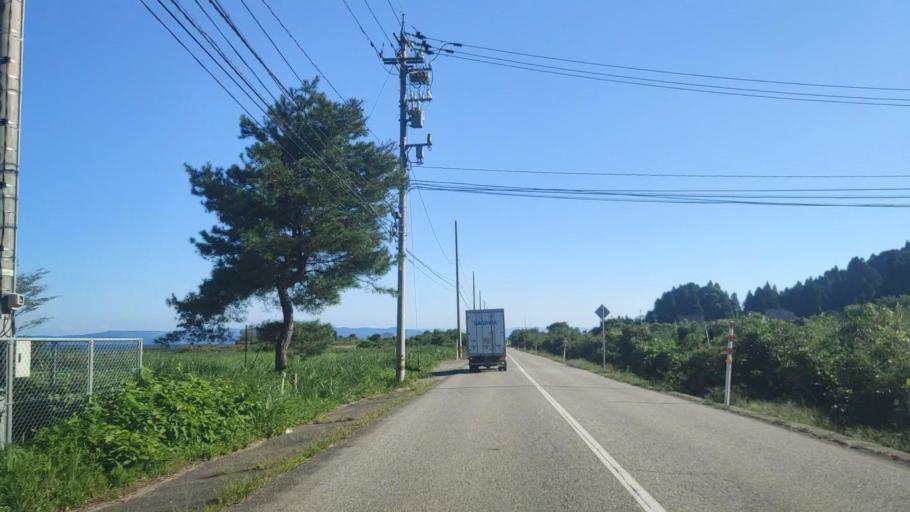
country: JP
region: Ishikawa
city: Nanao
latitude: 37.1978
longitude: 136.9099
